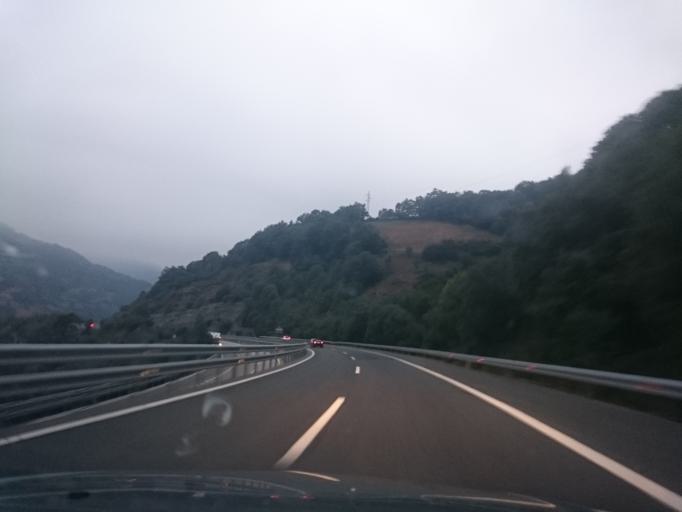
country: ES
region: Asturias
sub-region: Province of Asturias
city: Pola de Lena
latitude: 43.0543
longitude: -5.8201
